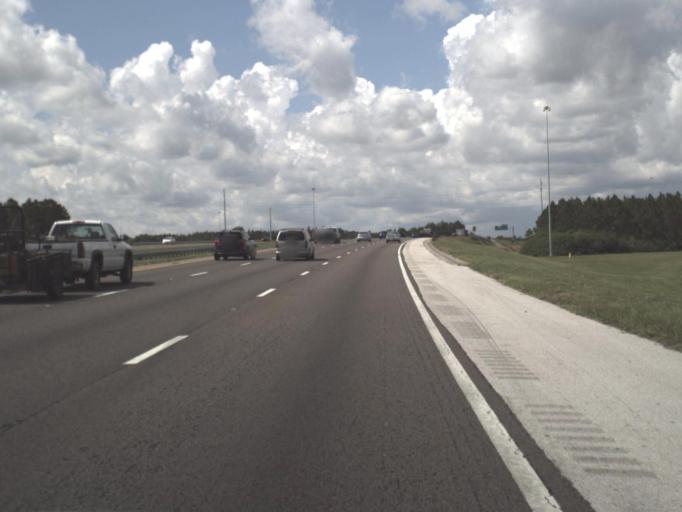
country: US
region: Florida
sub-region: Hillsborough County
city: Sun City Center
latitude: 27.7165
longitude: -82.3838
